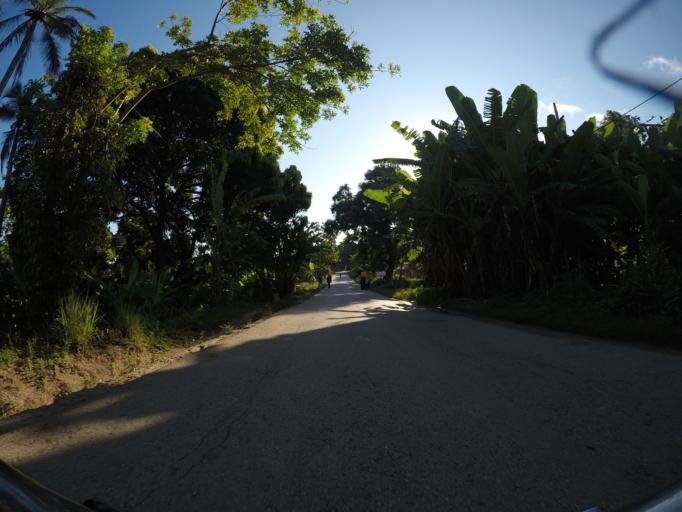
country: TZ
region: Pemba South
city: Mtambile
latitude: -5.3210
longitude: 39.7419
